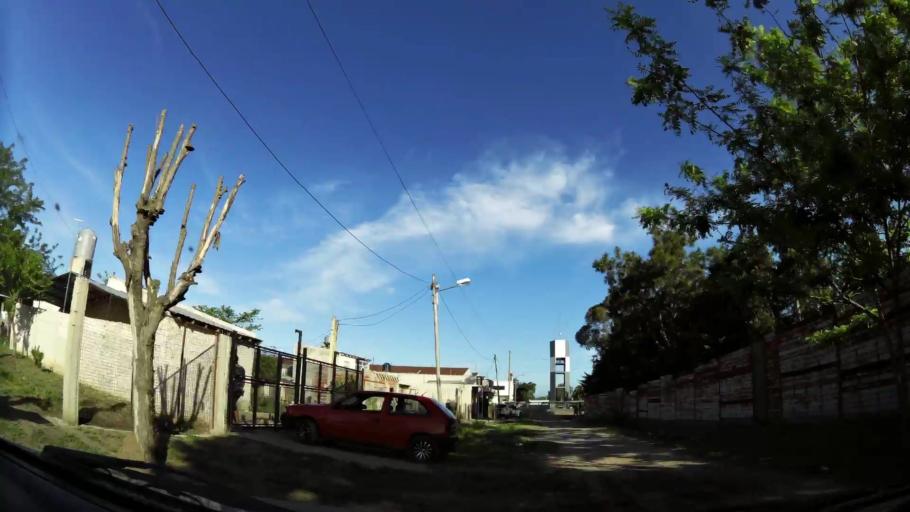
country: AR
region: Buenos Aires
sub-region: Partido de Quilmes
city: Quilmes
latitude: -34.8218
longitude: -58.2210
